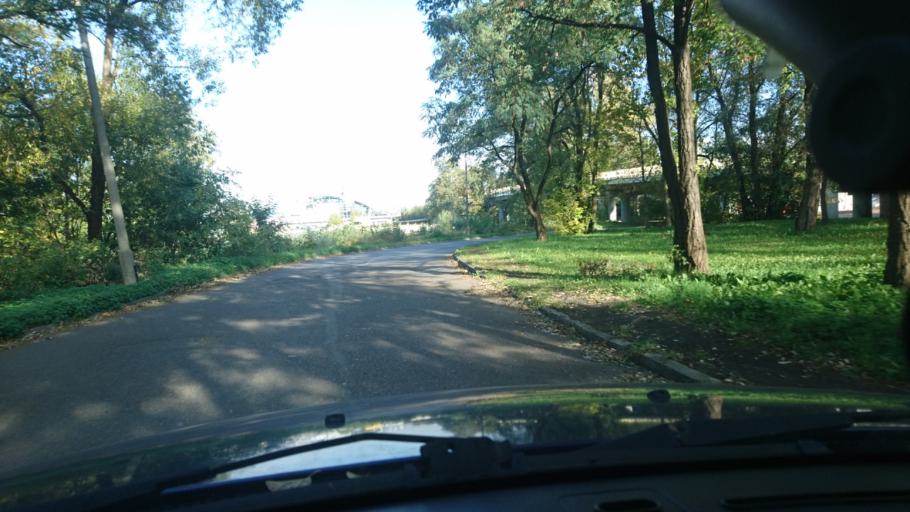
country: PL
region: Silesian Voivodeship
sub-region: Bielsko-Biala
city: Bielsko-Biala
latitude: 49.8369
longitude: 19.0395
